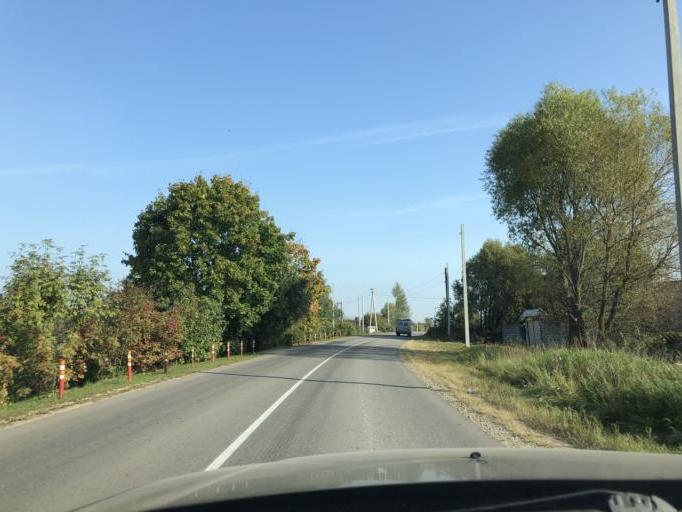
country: RU
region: Tula
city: Novogurovskiy
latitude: 54.4114
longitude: 37.3104
